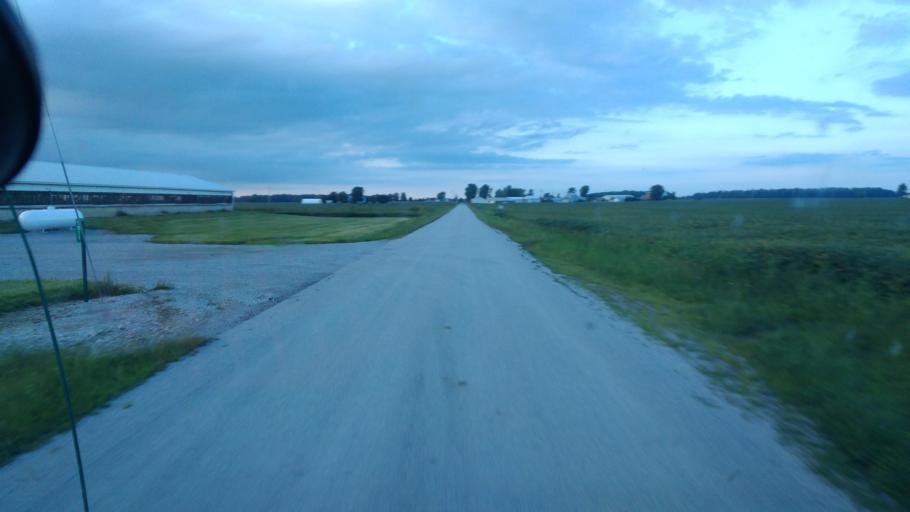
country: US
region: Ohio
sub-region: Hardin County
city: Kenton
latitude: 40.6749
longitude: -83.5145
